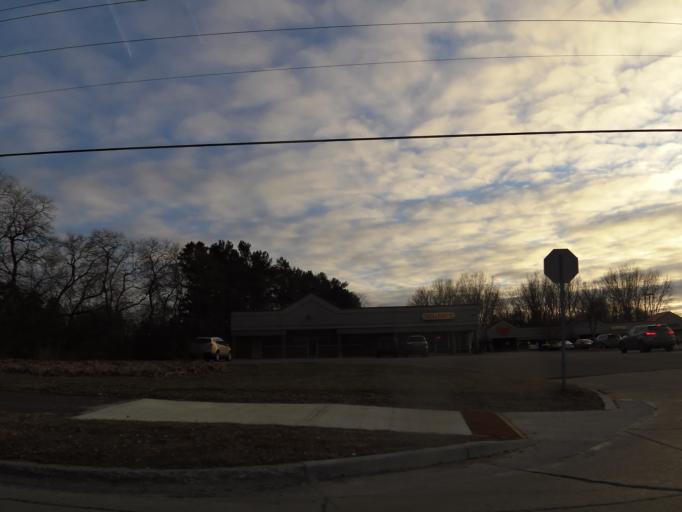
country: US
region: Minnesota
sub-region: Ramsey County
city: White Bear Lake
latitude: 45.0791
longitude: -93.0430
